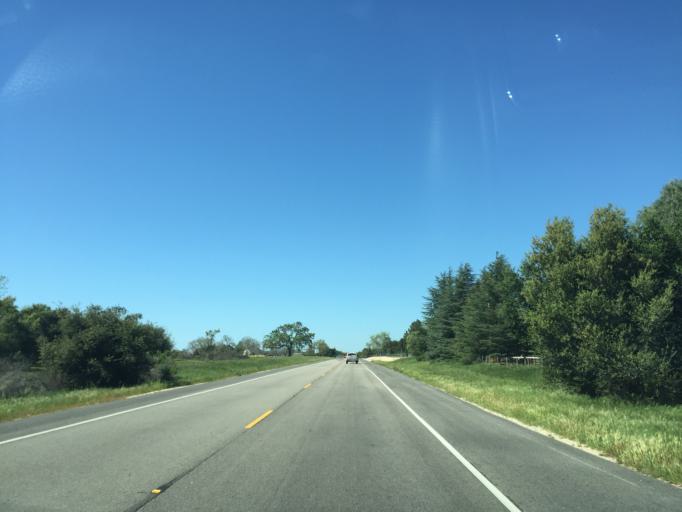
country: US
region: California
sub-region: Santa Barbara County
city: Santa Ynez
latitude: 34.6380
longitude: -120.0846
